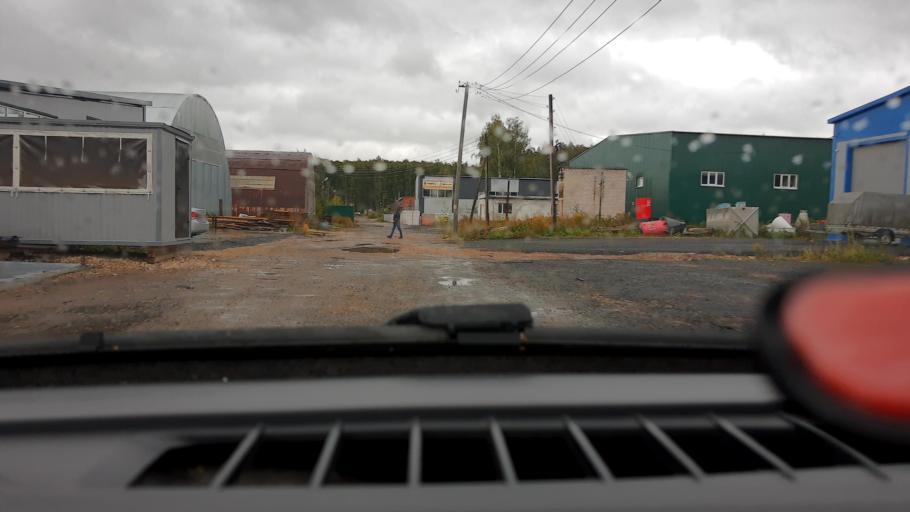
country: RU
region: Nizjnij Novgorod
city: Afonino
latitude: 56.1869
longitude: 44.1218
